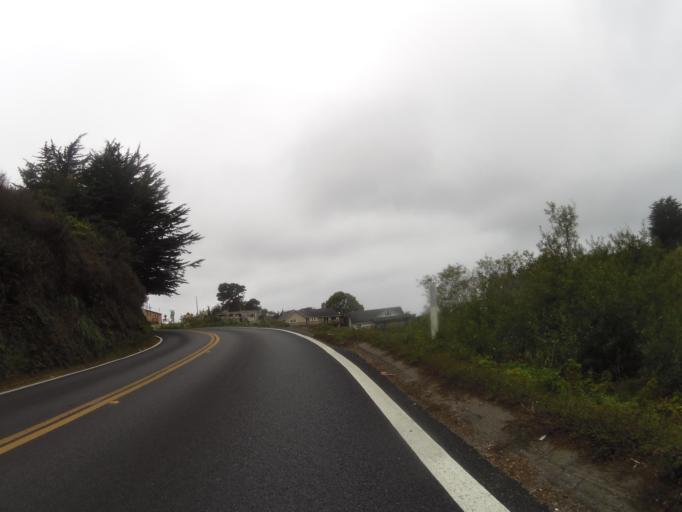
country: US
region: California
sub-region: Sonoma County
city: Bodega Bay
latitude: 38.3350
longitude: -123.0451
